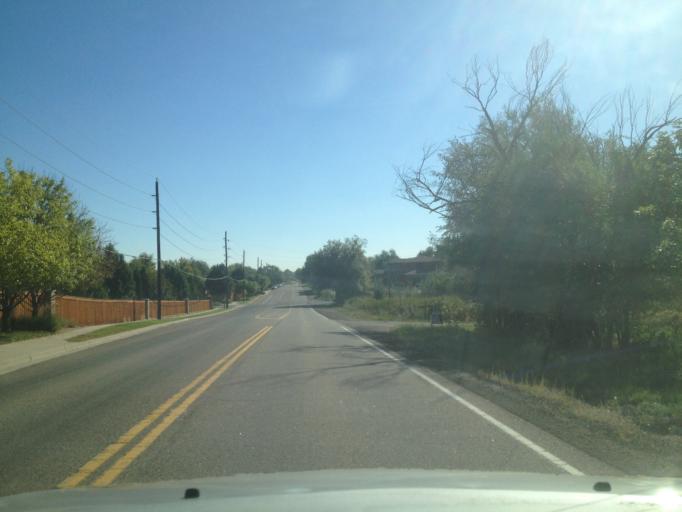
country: US
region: Colorado
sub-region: Jefferson County
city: Applewood
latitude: 39.7617
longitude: -105.1671
